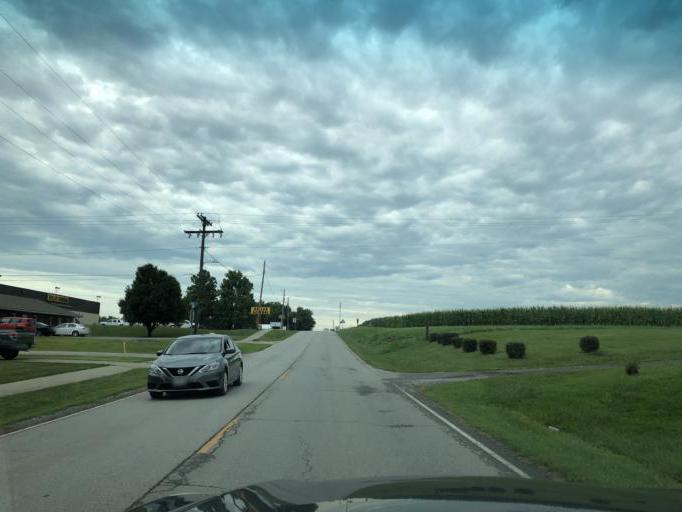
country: US
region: Missouri
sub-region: Saline County
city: Sweet Springs
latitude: 38.9721
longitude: -93.4152
